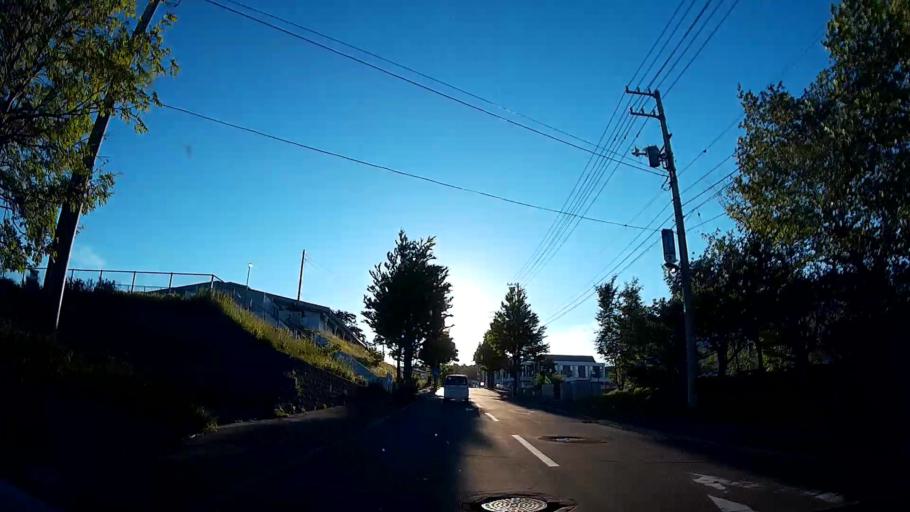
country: JP
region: Hokkaido
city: Otaru
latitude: 43.1657
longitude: 141.0403
